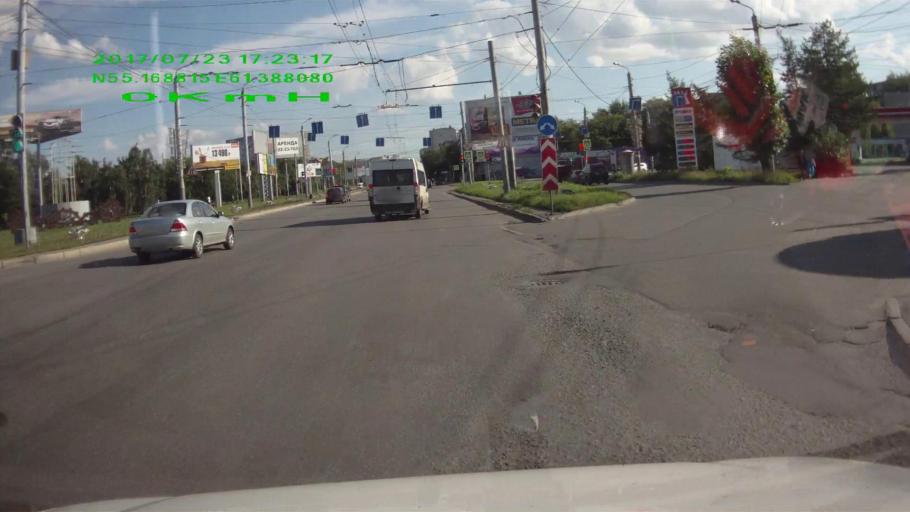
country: RU
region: Chelyabinsk
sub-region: Gorod Chelyabinsk
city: Chelyabinsk
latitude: 55.1687
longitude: 61.3882
